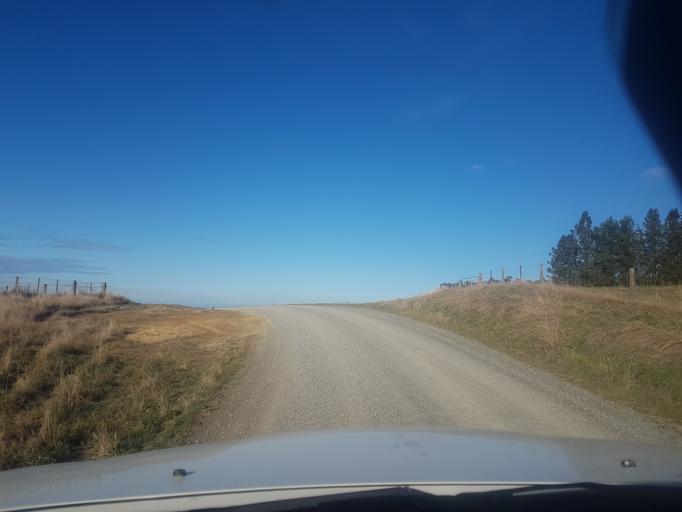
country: NZ
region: Canterbury
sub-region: Timaru District
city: Pleasant Point
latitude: -44.1671
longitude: 170.9018
